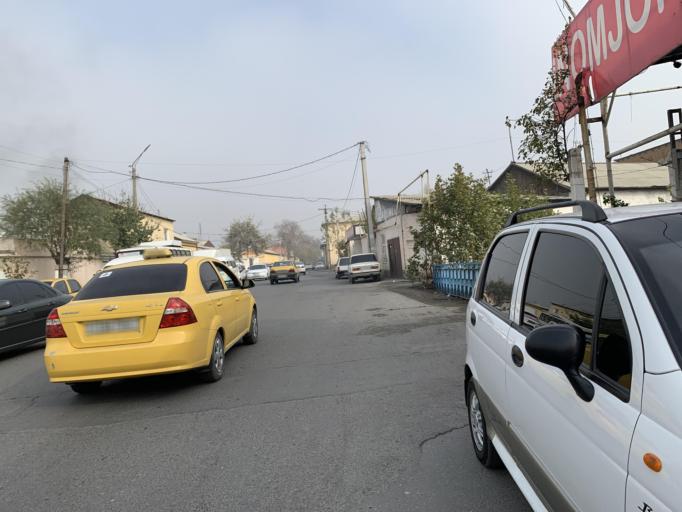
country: UZ
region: Fergana
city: Qo`qon
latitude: 40.5441
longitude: 70.9519
